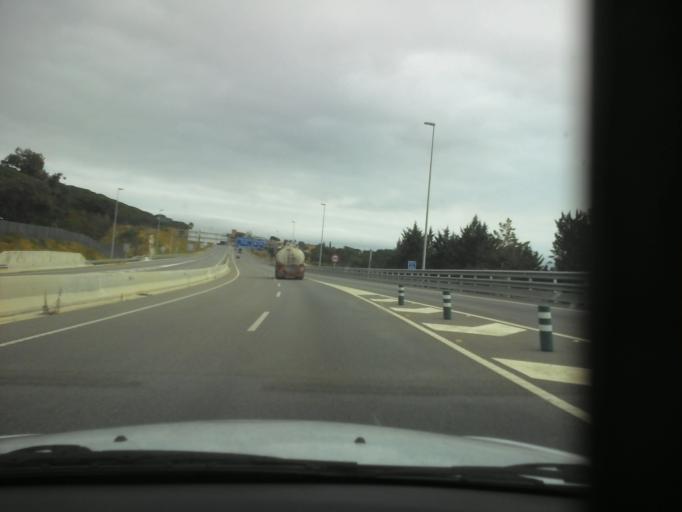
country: ES
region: Catalonia
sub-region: Provincia de Girona
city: Castell-Platja d'Aro
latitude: 41.8191
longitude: 3.0526
